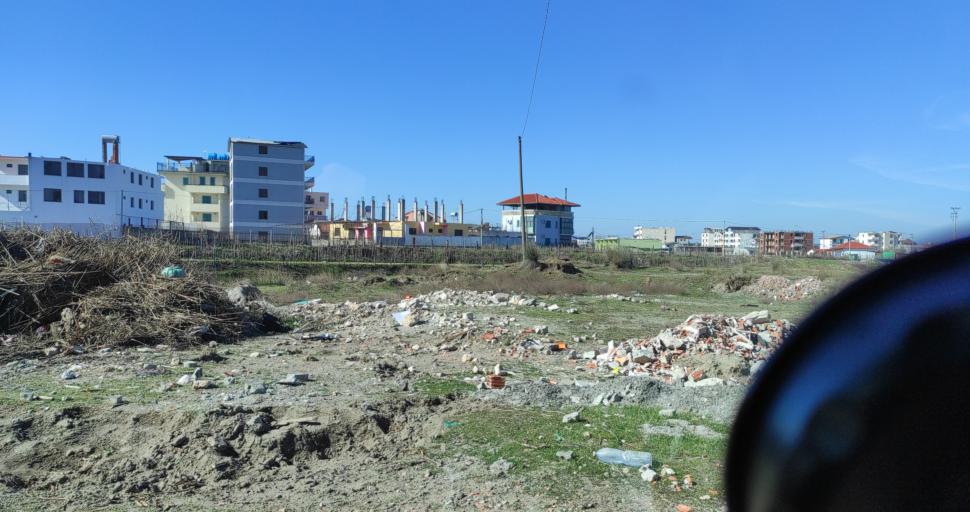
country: AL
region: Shkoder
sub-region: Rrethi i Shkodres
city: Velipoje
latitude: 41.8644
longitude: 19.4423
